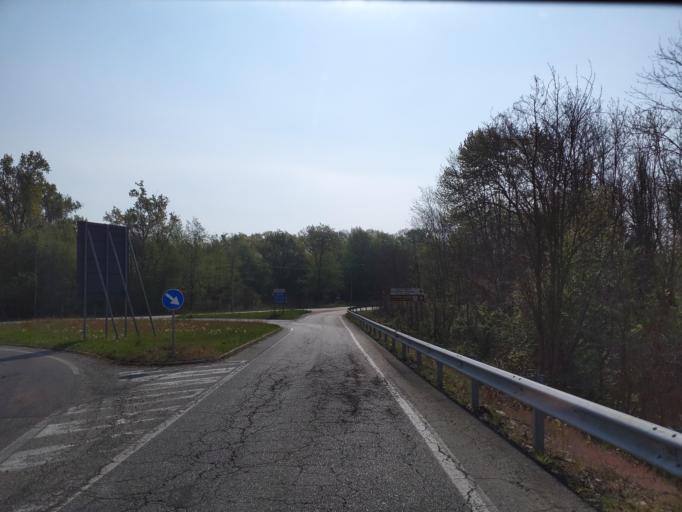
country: IT
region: Piedmont
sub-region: Provincia di Biella
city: Cossato
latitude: 45.5516
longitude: 8.2072
